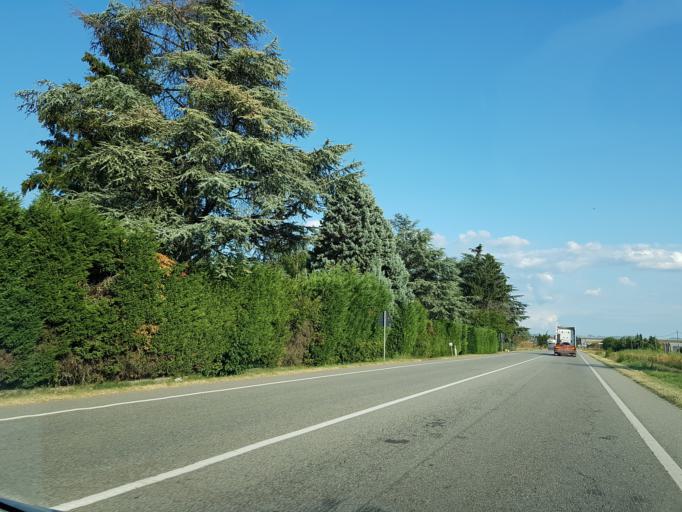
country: IT
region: Piedmont
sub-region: Provincia di Alessandria
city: Pozzolo Formigaro
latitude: 44.8125
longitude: 8.7623
